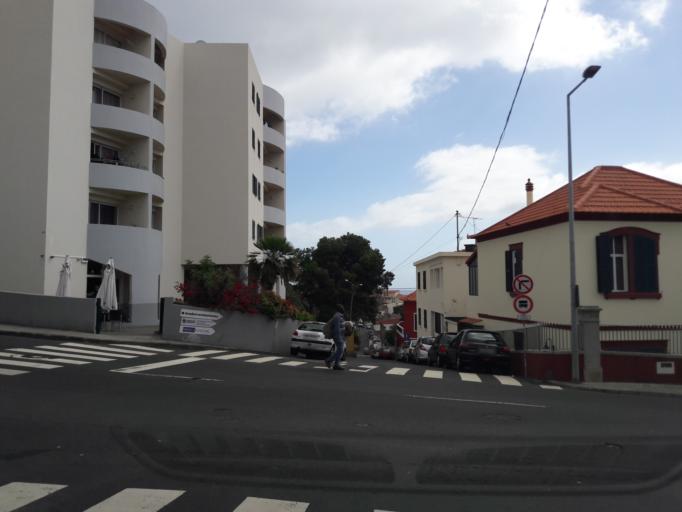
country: PT
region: Madeira
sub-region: Funchal
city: Nossa Senhora do Monte
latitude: 32.6511
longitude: -16.9003
